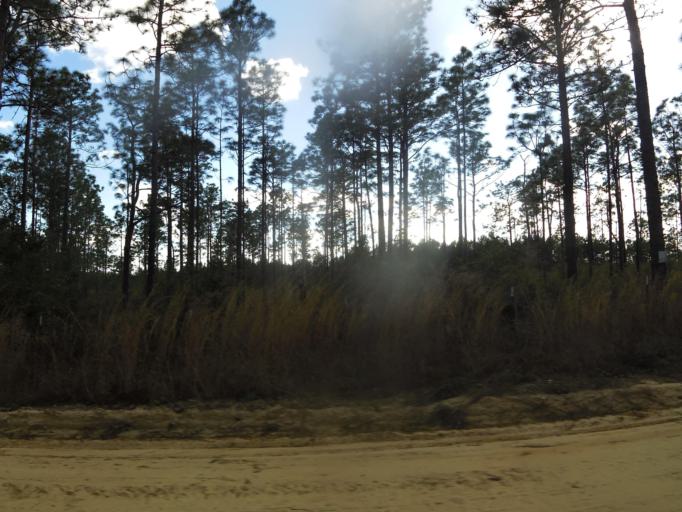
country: US
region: Florida
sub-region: Clay County
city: Keystone Heights
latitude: 29.7873
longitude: -81.8733
